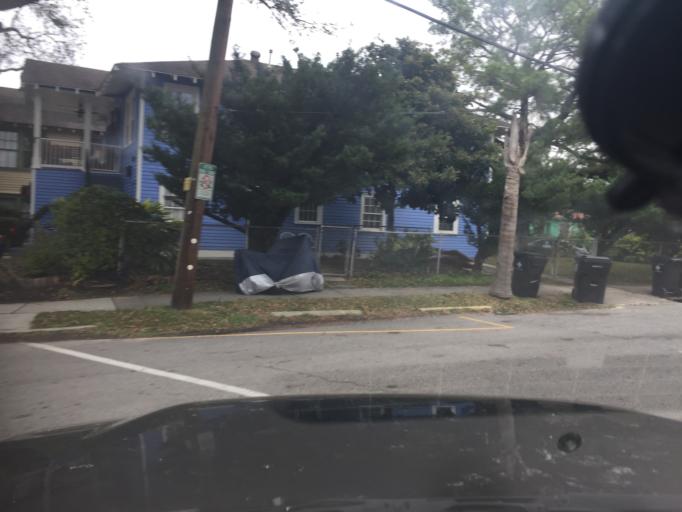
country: US
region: Louisiana
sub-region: Orleans Parish
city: New Orleans
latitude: 29.9851
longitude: -90.0764
